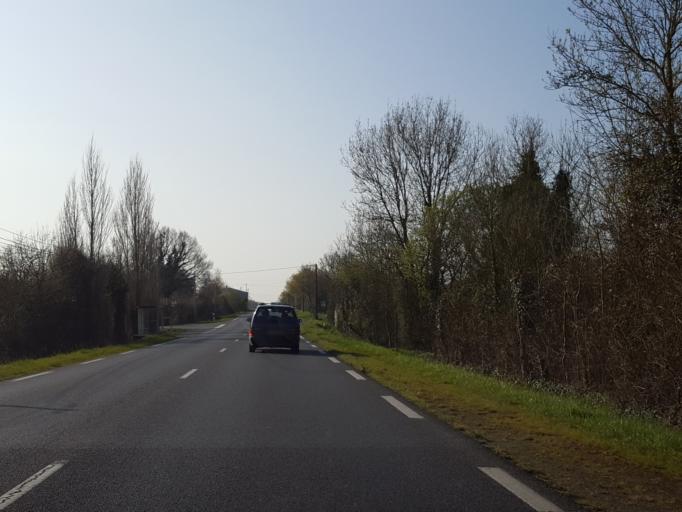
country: FR
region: Pays de la Loire
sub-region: Departement de la Loire-Atlantique
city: Le Bignon
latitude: 47.0980
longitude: -1.5330
